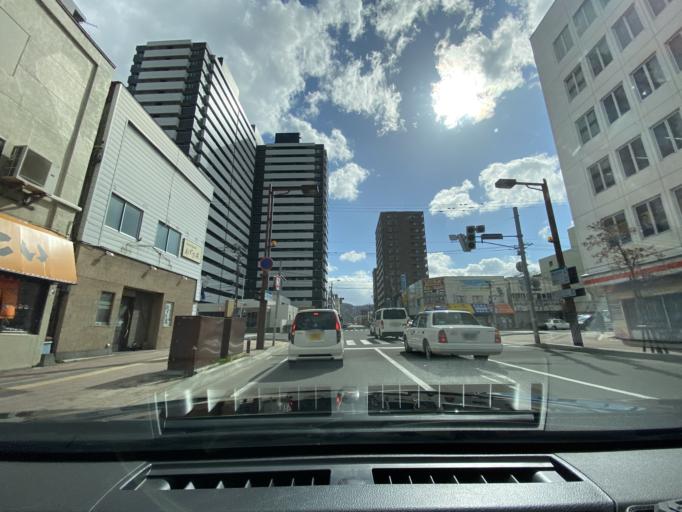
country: JP
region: Hokkaido
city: Sapporo
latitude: 43.0731
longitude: 141.3000
